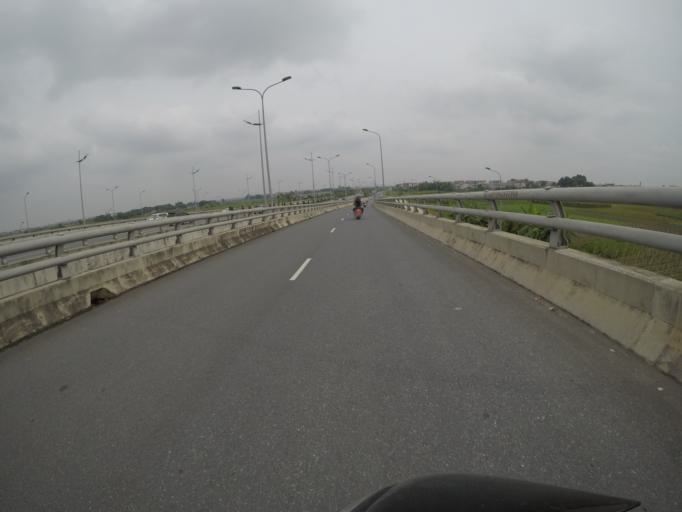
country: VN
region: Ha Noi
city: Dong Anh
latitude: 21.1664
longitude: 105.8205
